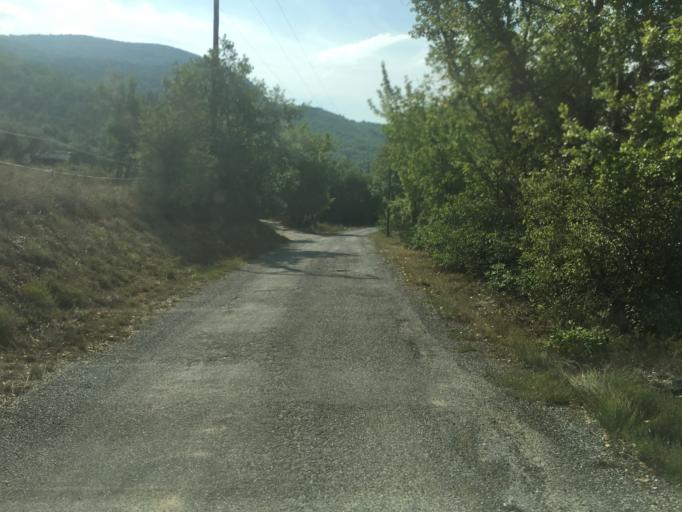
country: FR
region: Provence-Alpes-Cote d'Azur
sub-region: Departement des Alpes-de-Haute-Provence
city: Mallemoisson
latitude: 43.9299
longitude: 6.1889
